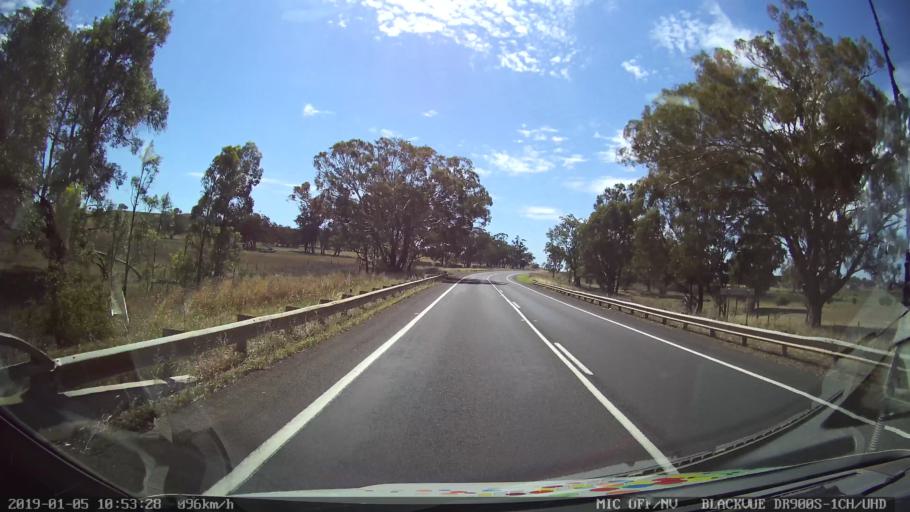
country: AU
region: New South Wales
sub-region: Warrumbungle Shire
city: Coonabarabran
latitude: -31.4426
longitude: 149.1145
